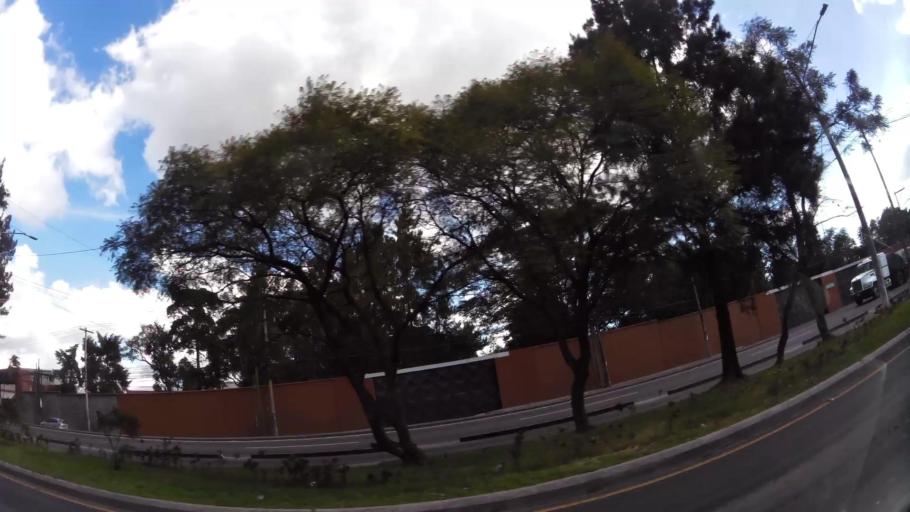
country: GT
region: Guatemala
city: Villa Nueva
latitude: 14.5854
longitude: -90.5640
